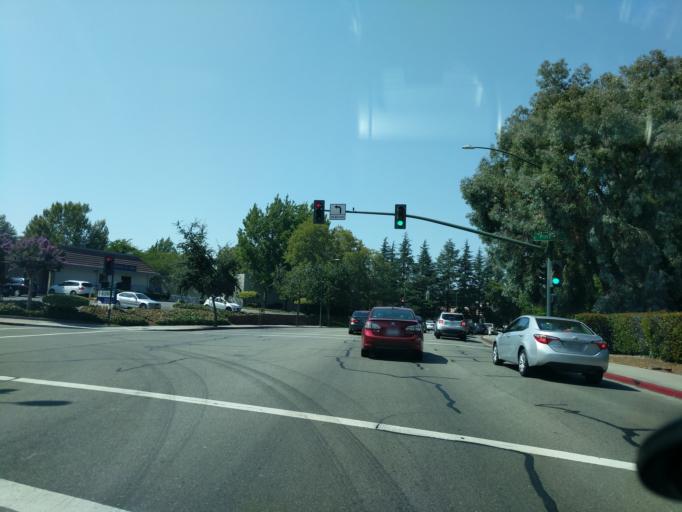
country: US
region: California
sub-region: Contra Costa County
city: Walnut Creek
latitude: 37.9108
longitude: -122.0597
